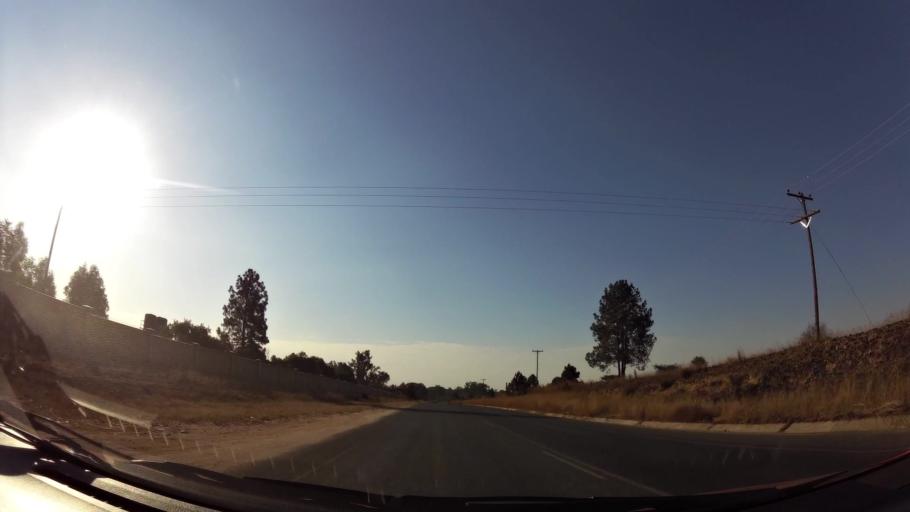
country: ZA
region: Gauteng
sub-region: West Rand District Municipality
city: Muldersdriseloop
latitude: -26.0092
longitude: 27.9097
